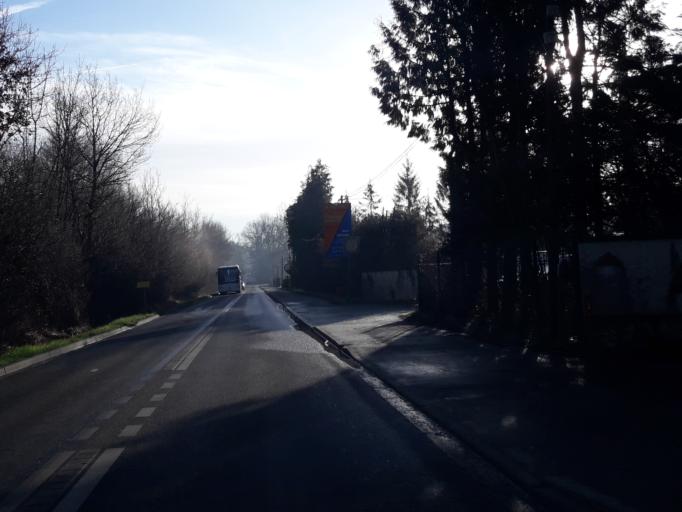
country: FR
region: Ile-de-France
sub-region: Departement de l'Essonne
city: Saint-Vrain
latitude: 48.5402
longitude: 2.3478
